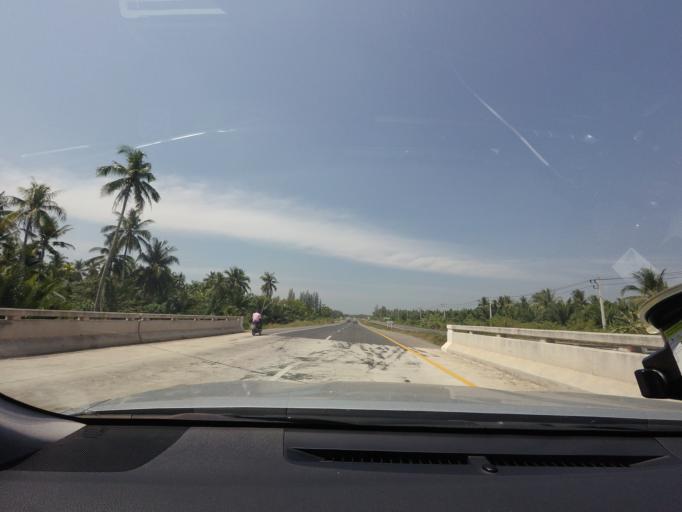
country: TH
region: Surat Thani
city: Surat Thani
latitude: 9.1765
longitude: 99.3051
